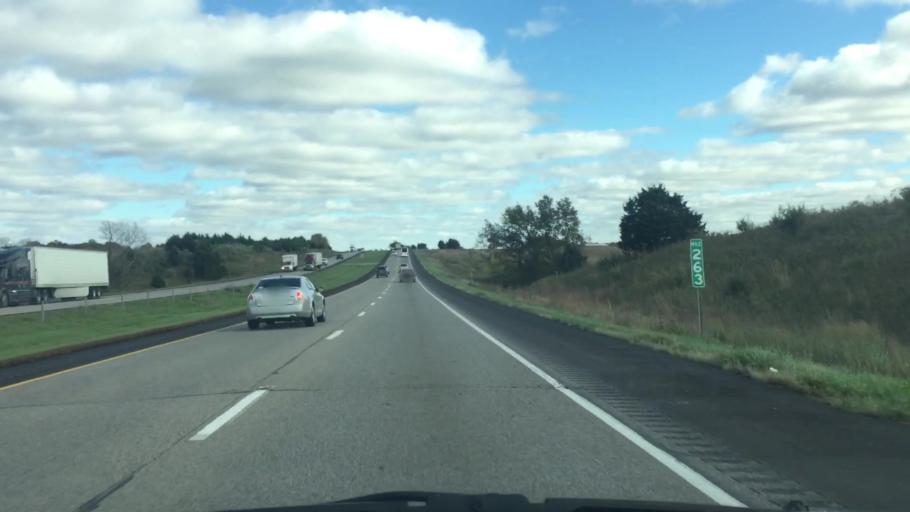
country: US
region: Iowa
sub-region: Muscatine County
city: West Liberty
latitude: 41.6538
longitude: -91.1871
